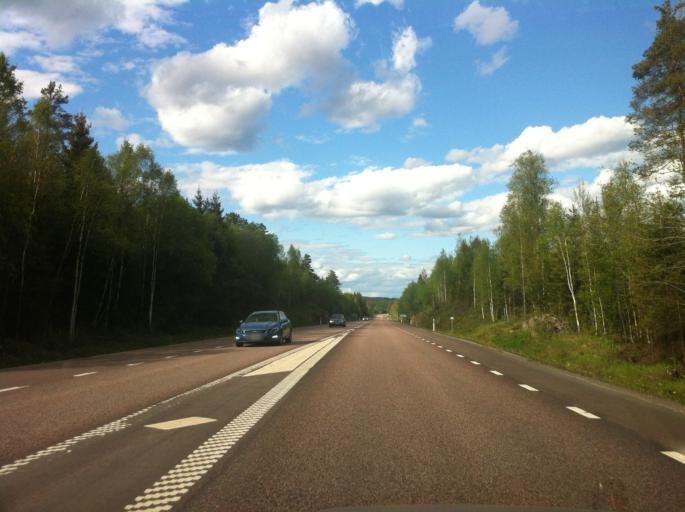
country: SE
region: Vaermland
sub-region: Filipstads Kommun
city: Filipstad
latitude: 59.7148
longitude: 14.1891
